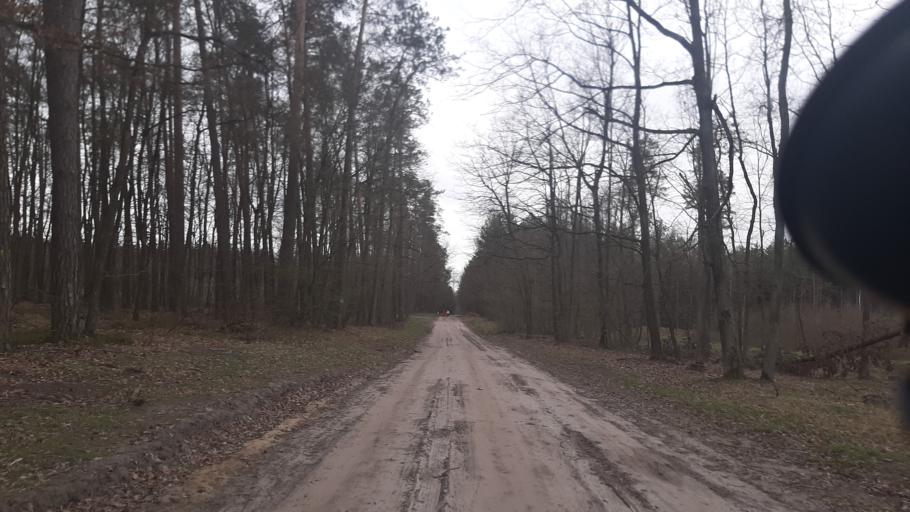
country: PL
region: Lublin Voivodeship
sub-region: Powiat lubartowski
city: Lubartow
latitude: 51.3941
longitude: 22.5669
